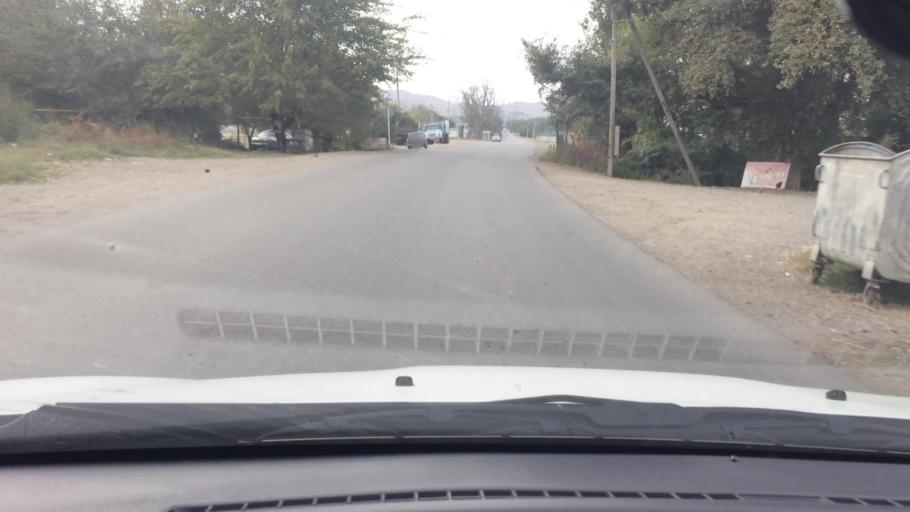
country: GE
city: Naghvarevi
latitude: 41.3544
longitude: 44.8594
